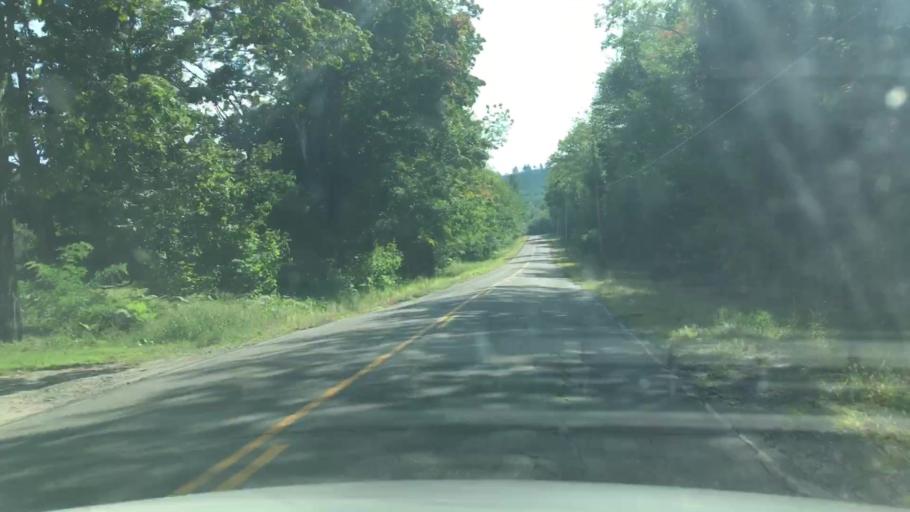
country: US
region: Maine
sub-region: Penobscot County
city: Enfield
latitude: 45.3008
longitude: -68.5502
